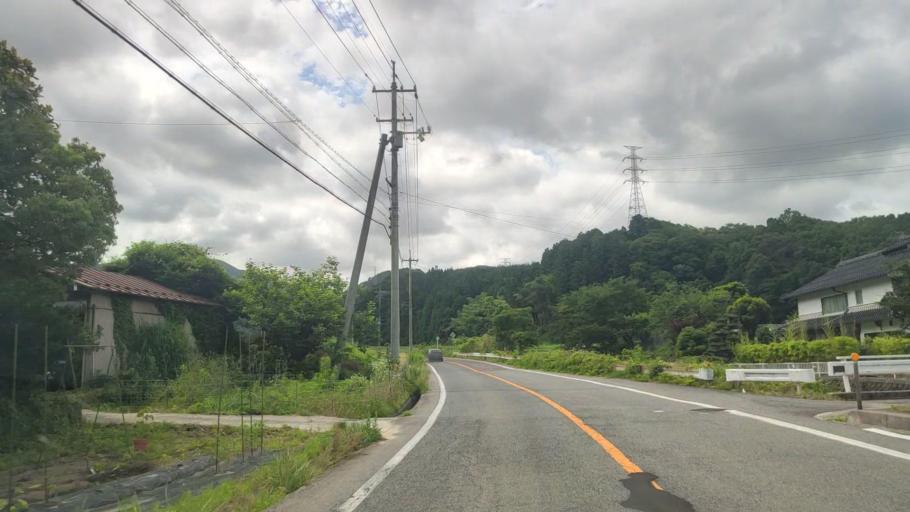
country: JP
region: Tottori
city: Yonago
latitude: 35.2967
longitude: 133.4148
